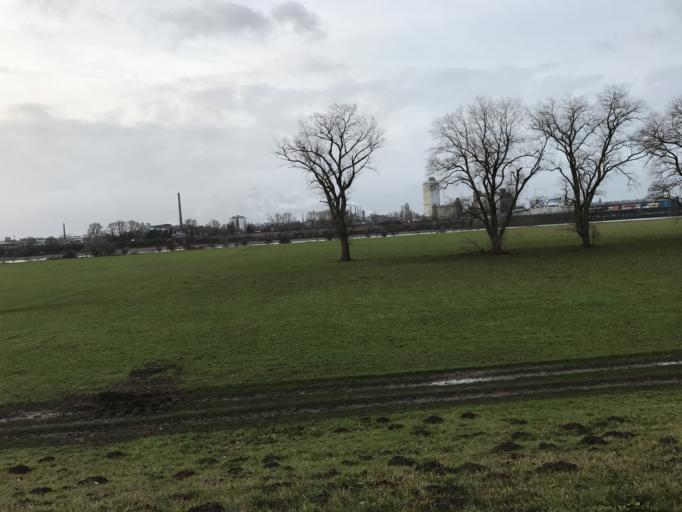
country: DE
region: North Rhine-Westphalia
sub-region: Regierungsbezirk Dusseldorf
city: Krefeld
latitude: 51.3500
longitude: 6.6724
